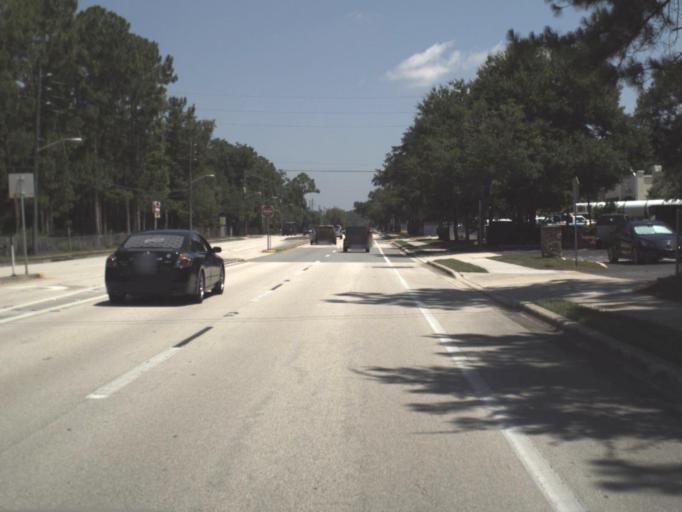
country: US
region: Florida
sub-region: Saint Johns County
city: Fruit Cove
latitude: 30.1136
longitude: -81.6260
